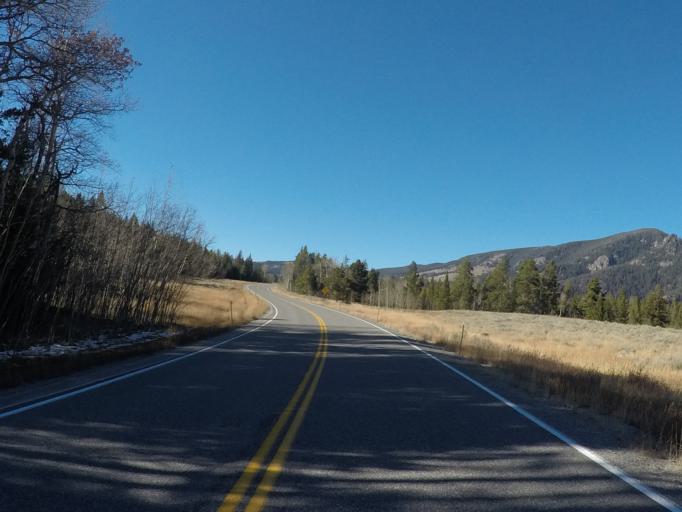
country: US
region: Montana
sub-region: Carbon County
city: Red Lodge
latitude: 44.8577
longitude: -109.5136
